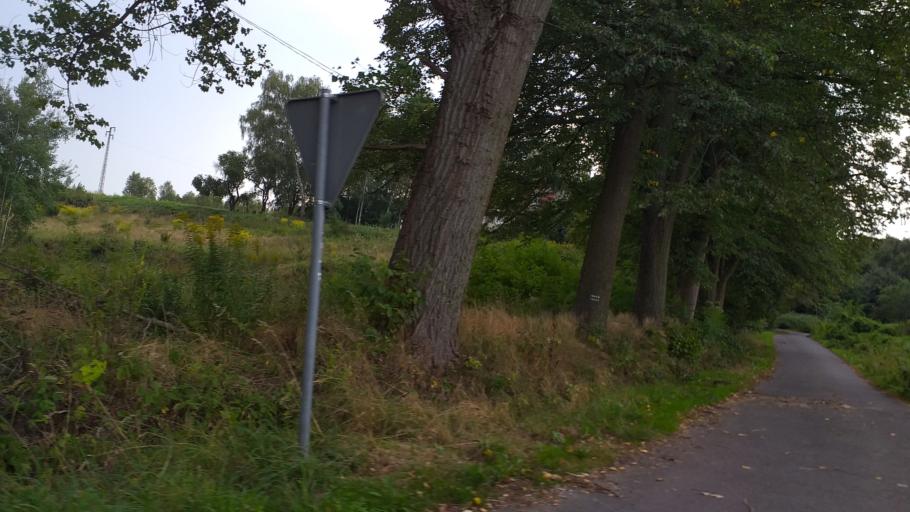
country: PL
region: Lower Silesian Voivodeship
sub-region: Powiat lubanski
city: Lesna
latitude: 51.0440
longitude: 15.2574
